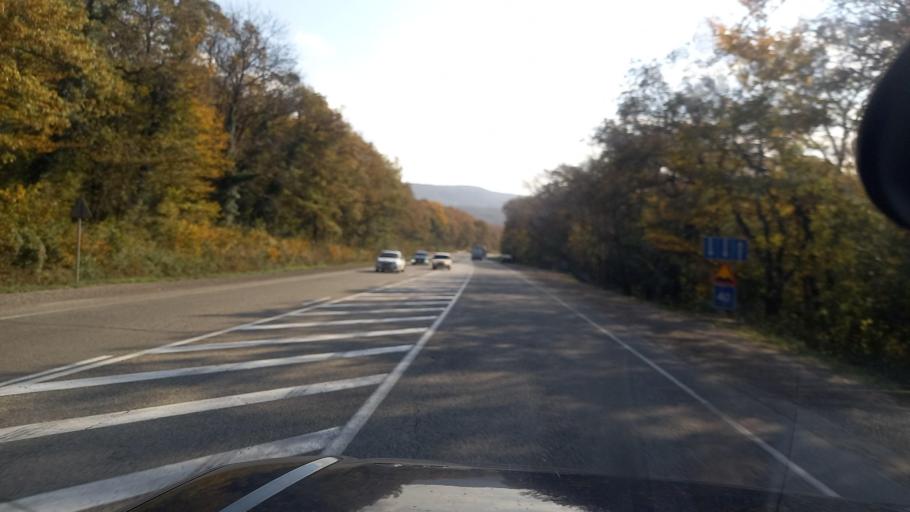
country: RU
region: Krasnodarskiy
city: Verkhnebakanskiy
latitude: 44.8430
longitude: 37.6987
